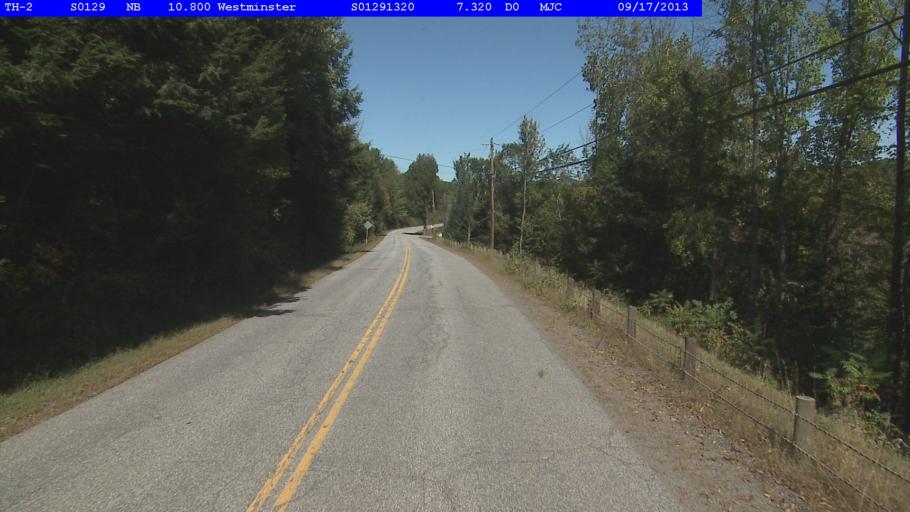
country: US
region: Vermont
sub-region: Windham County
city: Rockingham
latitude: 43.1191
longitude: -72.5326
